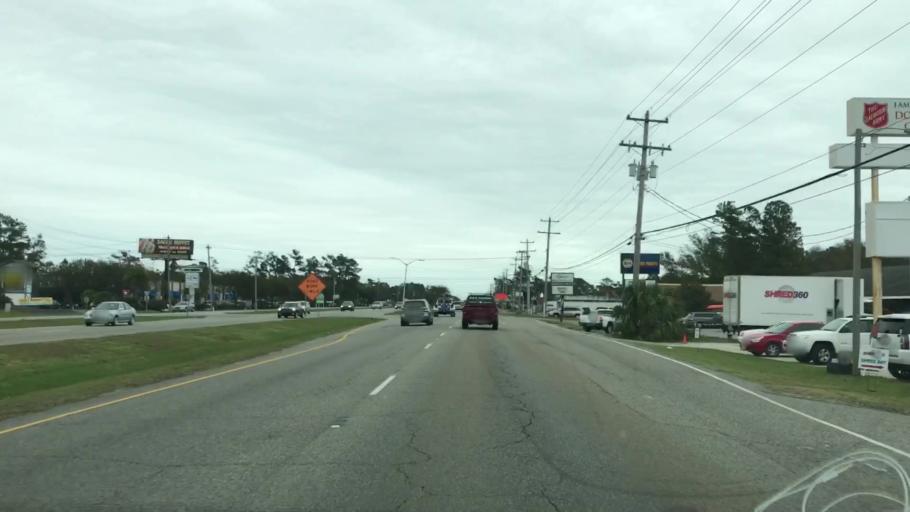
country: US
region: South Carolina
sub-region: Horry County
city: Surfside Beach
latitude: 33.6056
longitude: -78.9882
